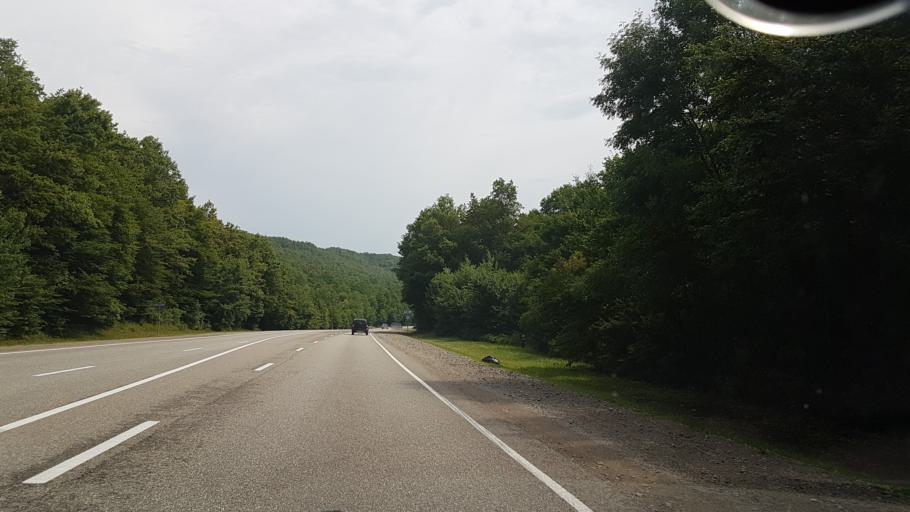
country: RU
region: Krasnodarskiy
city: Goryachiy Klyuch
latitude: 44.5392
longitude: 38.9507
